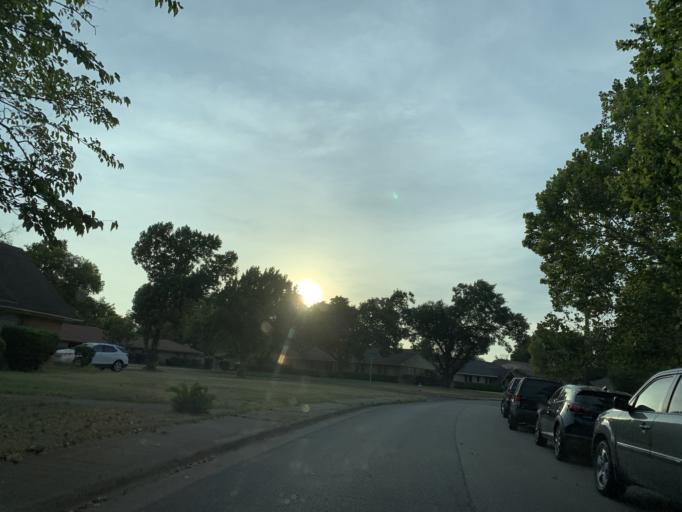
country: US
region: Texas
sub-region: Dallas County
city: Cockrell Hill
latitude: 32.6941
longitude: -96.8843
